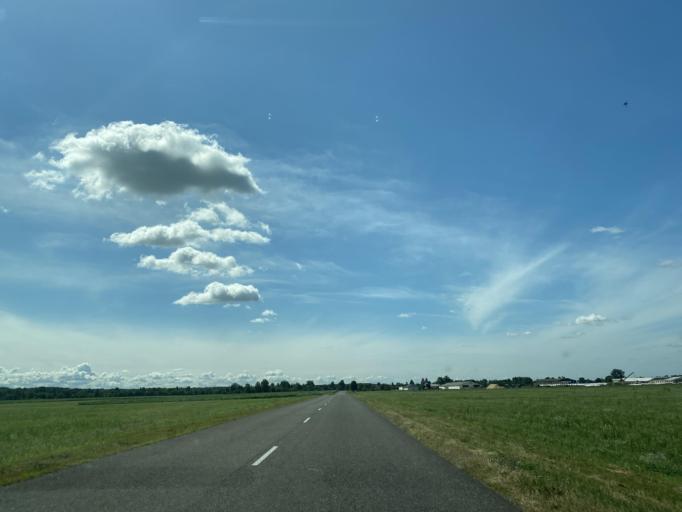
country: BY
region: Brest
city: Ivanava
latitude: 52.2151
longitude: 25.6298
